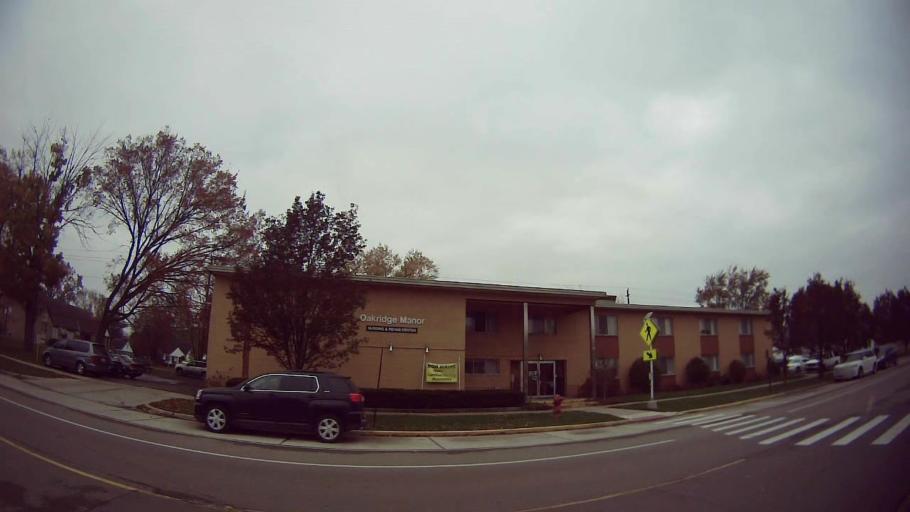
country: US
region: Michigan
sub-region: Oakland County
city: Ferndale
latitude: 42.4729
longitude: -83.1236
